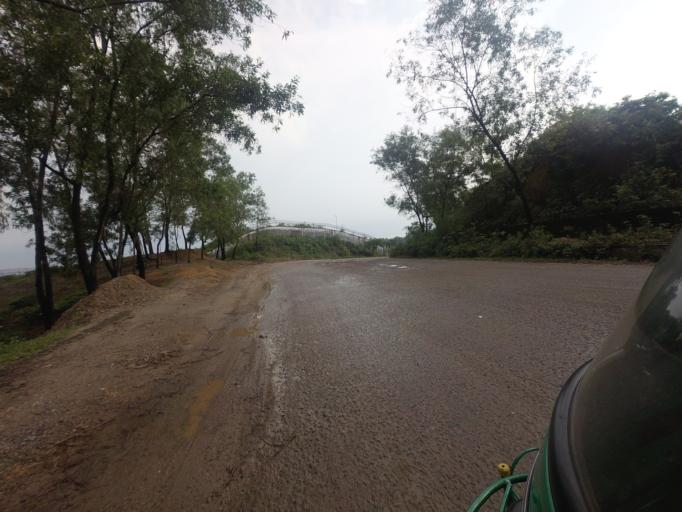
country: BD
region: Sylhet
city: Sylhet
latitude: 24.9554
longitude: 91.8799
